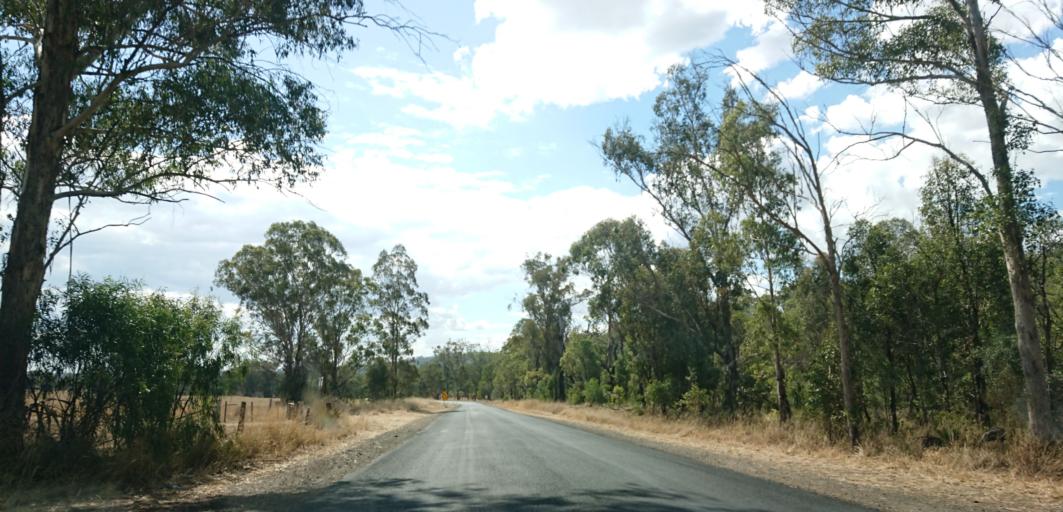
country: AU
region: Queensland
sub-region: Toowoomba
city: Top Camp
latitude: -27.7981
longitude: 152.1046
